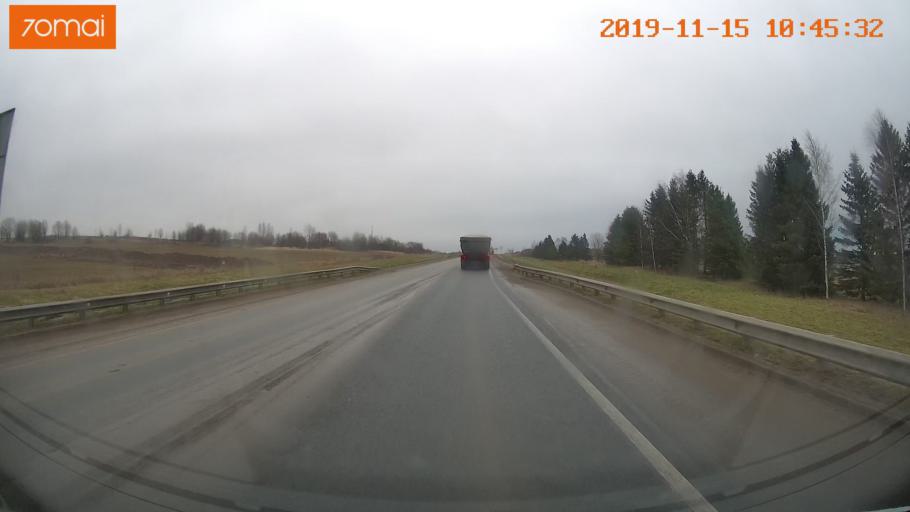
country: RU
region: Vologda
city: Sheksna
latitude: 59.2112
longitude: 38.5896
